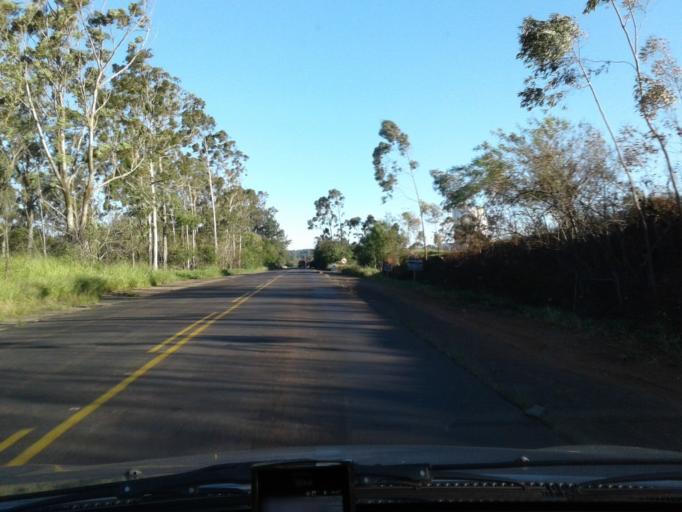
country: BR
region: Rio Grande do Sul
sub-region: Gravatai
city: Gravatai
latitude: -30.0048
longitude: -50.9932
